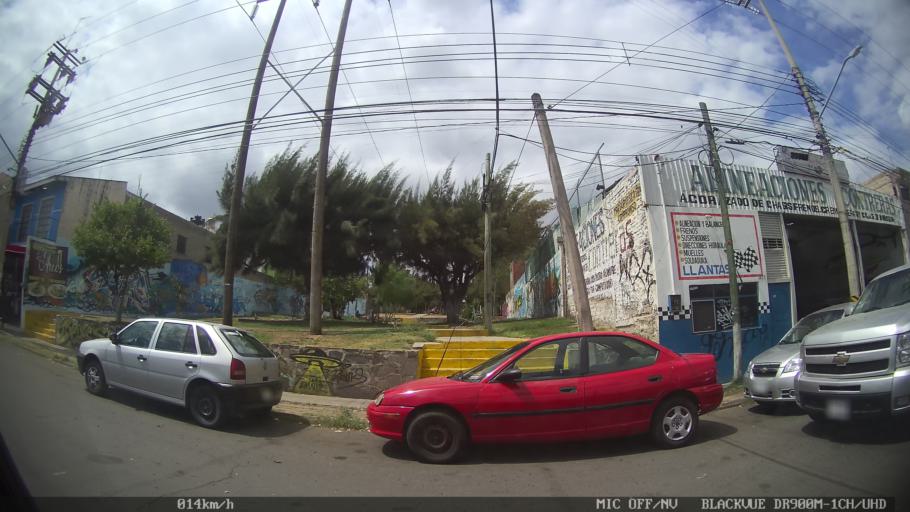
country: MX
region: Jalisco
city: Tlaquepaque
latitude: 20.6315
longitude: -103.2647
